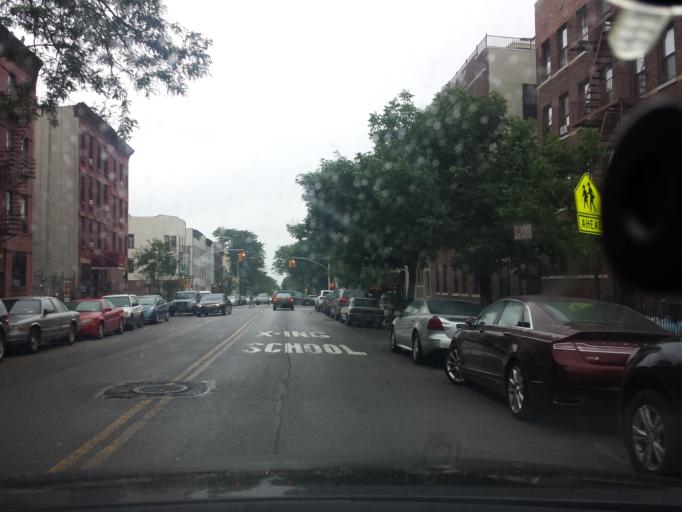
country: US
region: New York
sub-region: Kings County
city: Brooklyn
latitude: 40.6598
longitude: -73.9834
